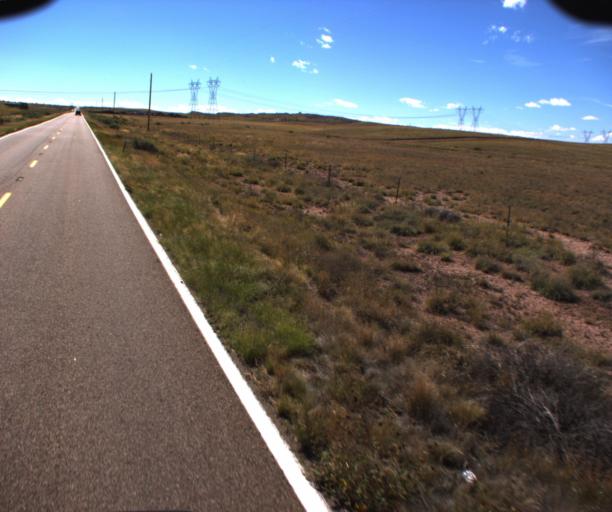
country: US
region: Arizona
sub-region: Apache County
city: Saint Johns
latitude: 34.5821
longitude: -109.3326
